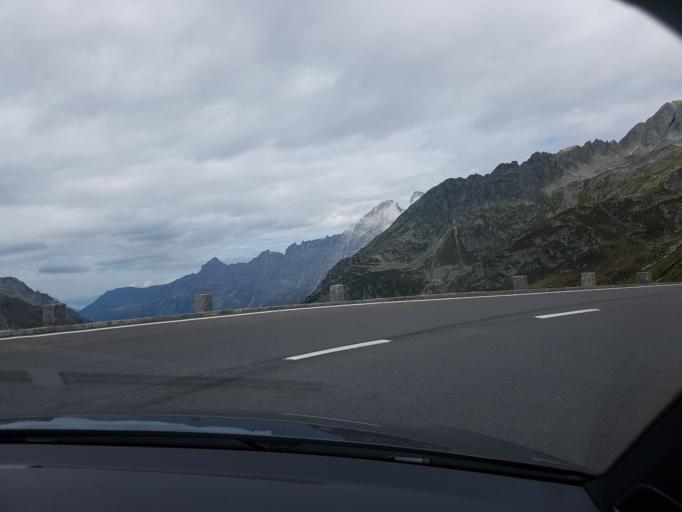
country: CH
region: Obwalden
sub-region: Obwalden
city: Engelberg
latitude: 46.7267
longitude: 8.4416
